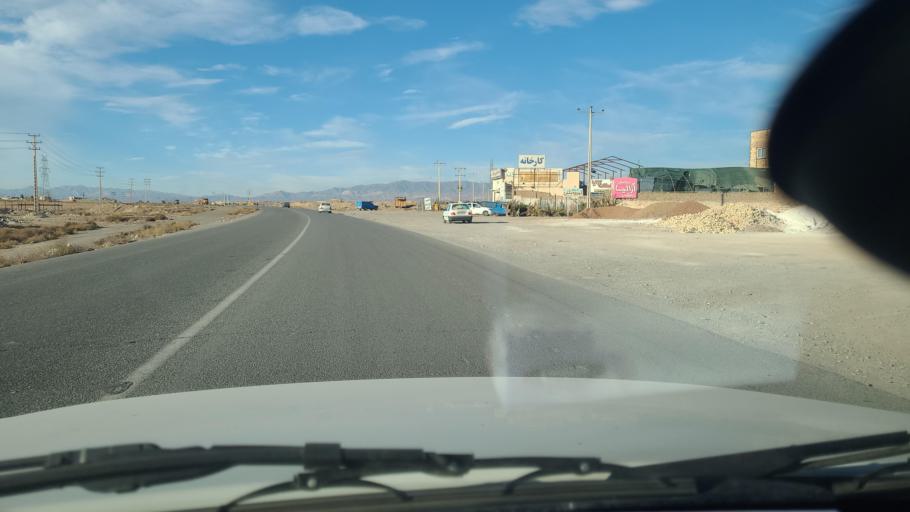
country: IR
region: Razavi Khorasan
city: Sabzevar
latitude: 36.2274
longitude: 57.6513
